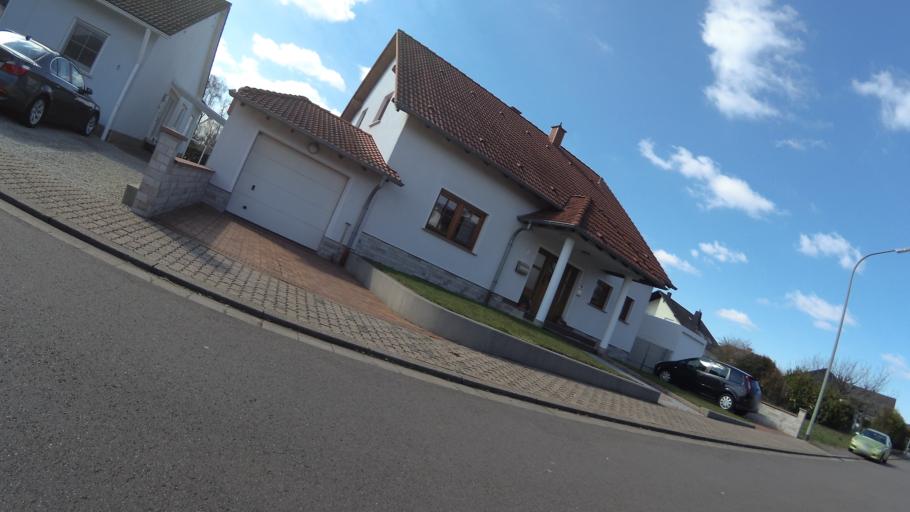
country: DE
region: Saarland
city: Beckingen
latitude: 49.3862
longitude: 6.7132
